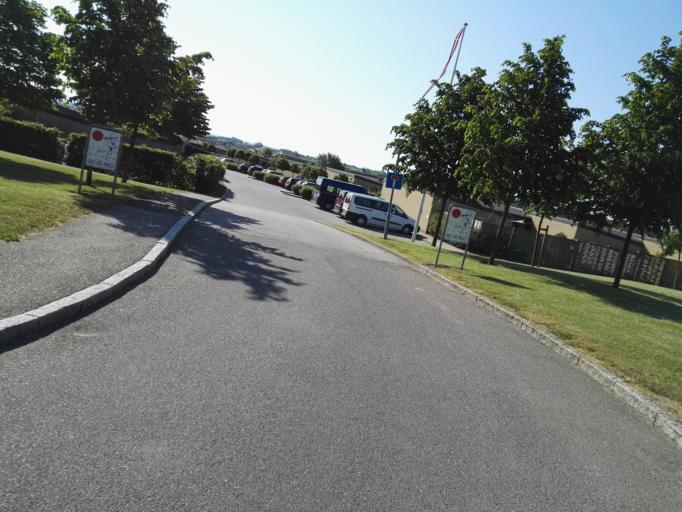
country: DK
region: Zealand
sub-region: Lejre Kommune
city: Ejby
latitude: 55.7009
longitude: 11.8926
